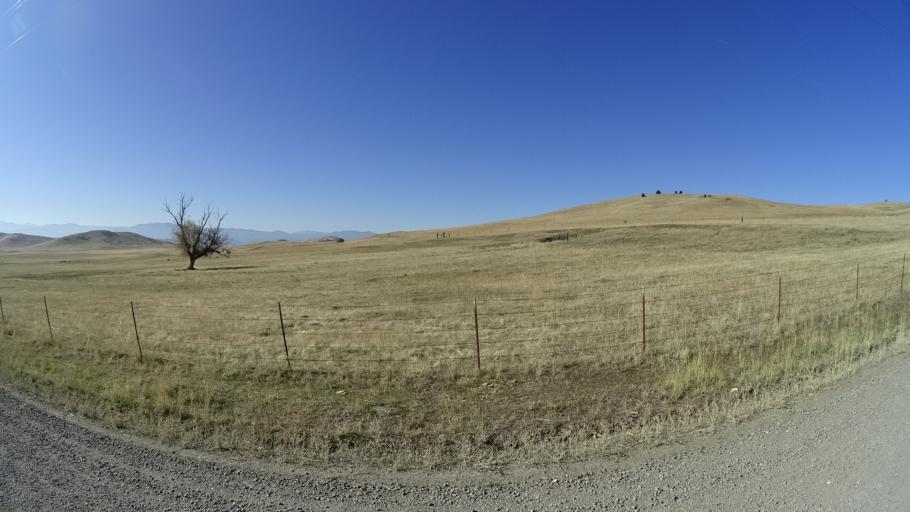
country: US
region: California
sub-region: Siskiyou County
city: Montague
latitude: 41.7616
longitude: -122.3593
